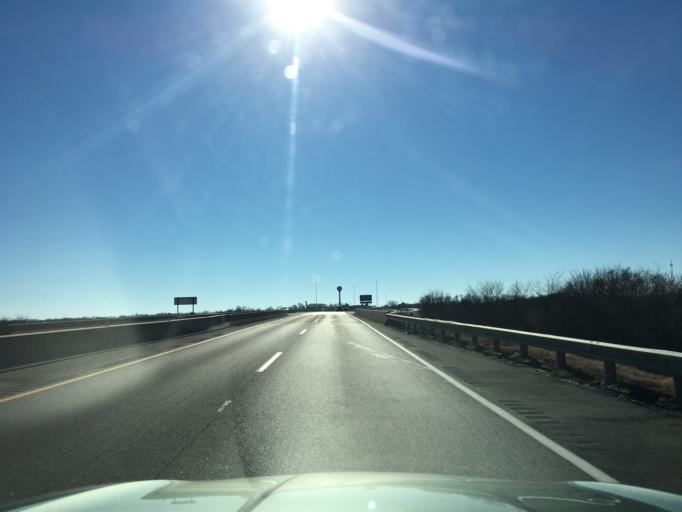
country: US
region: Kansas
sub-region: Sumner County
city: Belle Plaine
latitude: 37.3752
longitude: -97.3232
